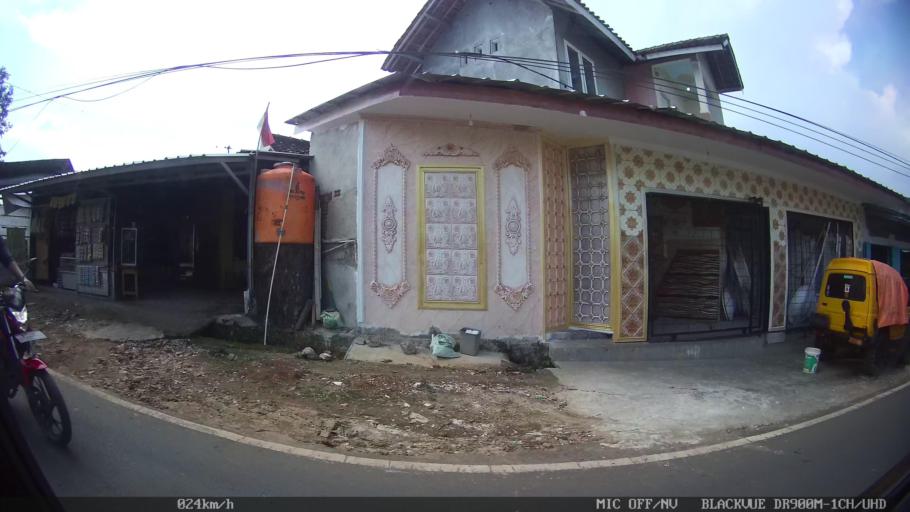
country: ID
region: Lampung
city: Bandarlampung
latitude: -5.4036
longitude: 105.2326
